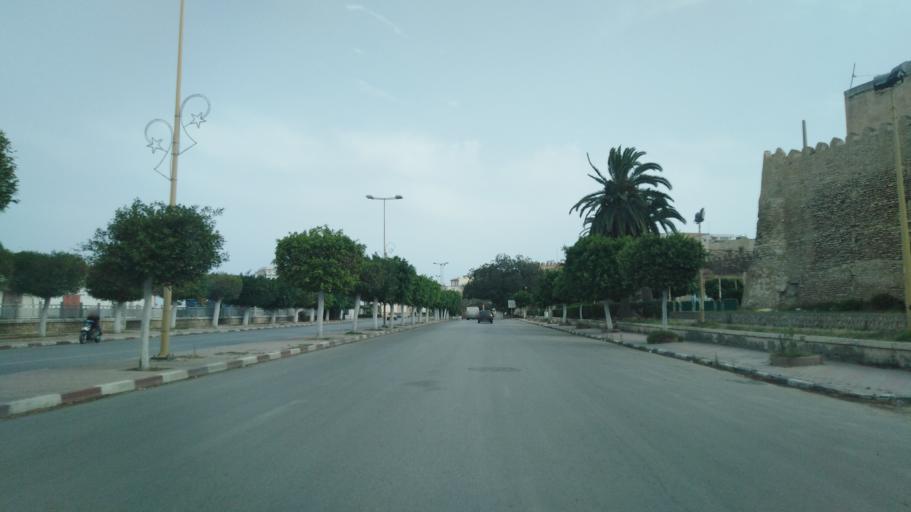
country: TN
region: Safaqis
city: Sfax
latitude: 34.7369
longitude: 10.7643
